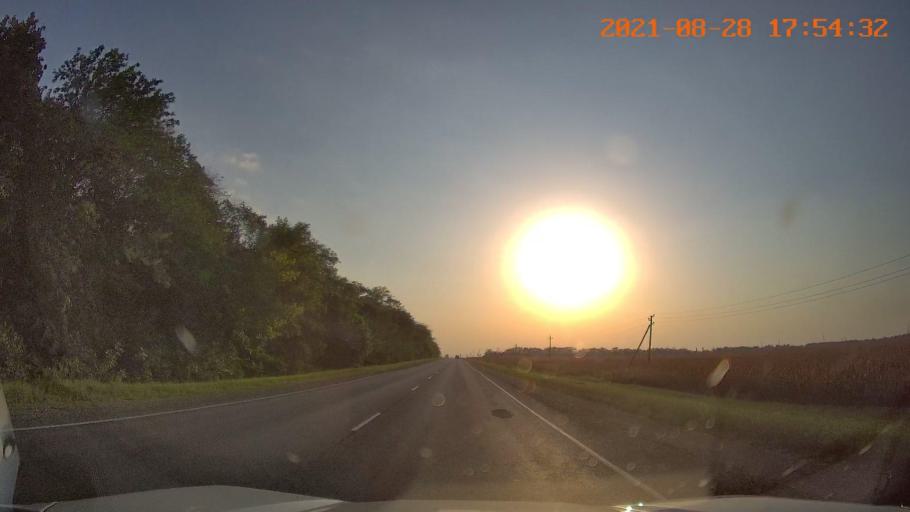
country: RU
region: Krasnodarskiy
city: Konstantinovskaya
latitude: 44.9352
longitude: 40.7328
